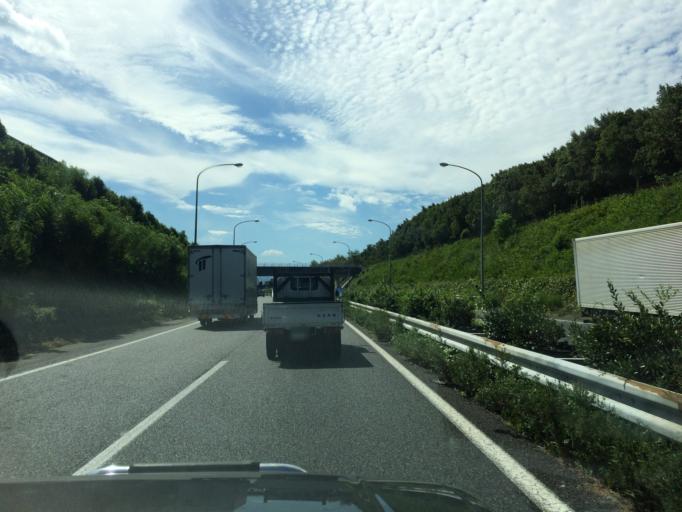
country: JP
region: Osaka
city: Izumi
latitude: 34.4880
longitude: 135.4656
